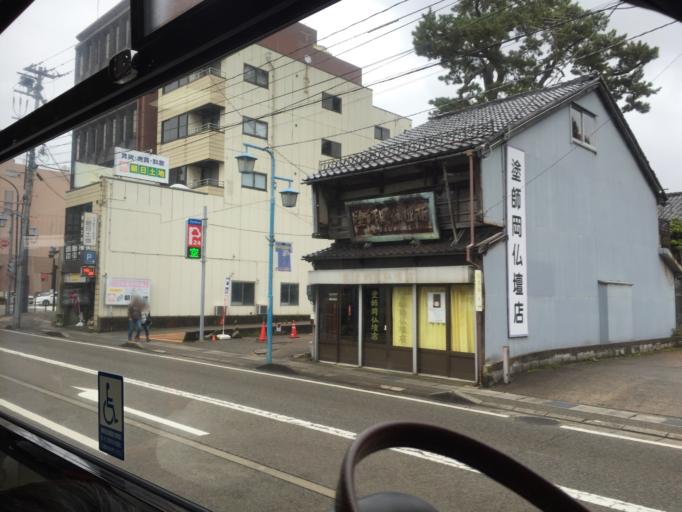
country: JP
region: Ishikawa
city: Nonoichi
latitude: 36.5565
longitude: 136.6486
